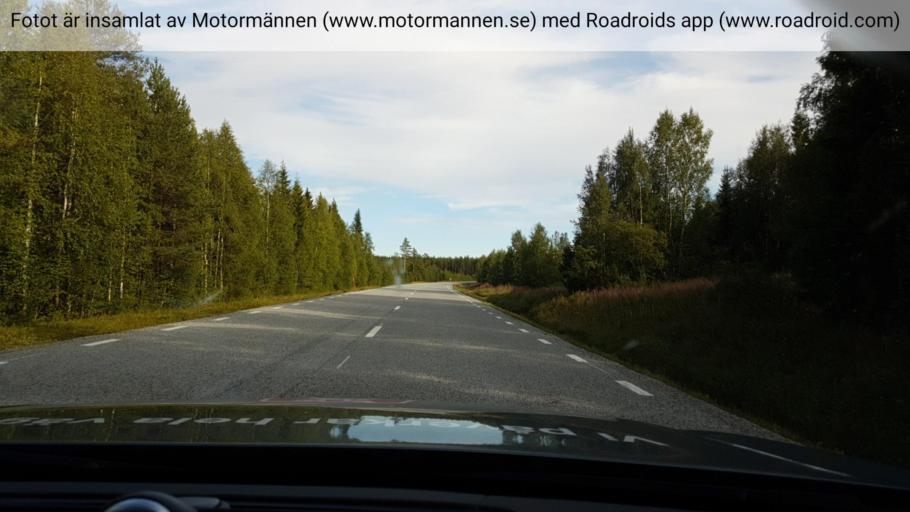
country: SE
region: Jaemtland
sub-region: Stroemsunds Kommun
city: Stroemsund
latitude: 64.2107
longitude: 15.5802
